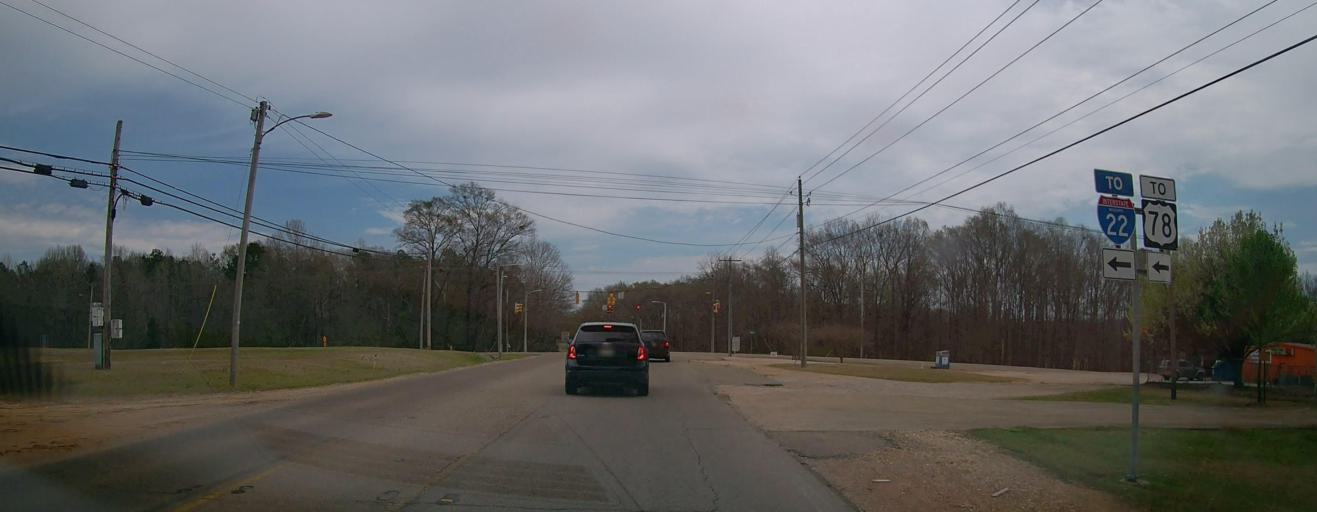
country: US
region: Mississippi
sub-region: Lee County
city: Plantersville
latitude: 34.2580
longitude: -88.6577
